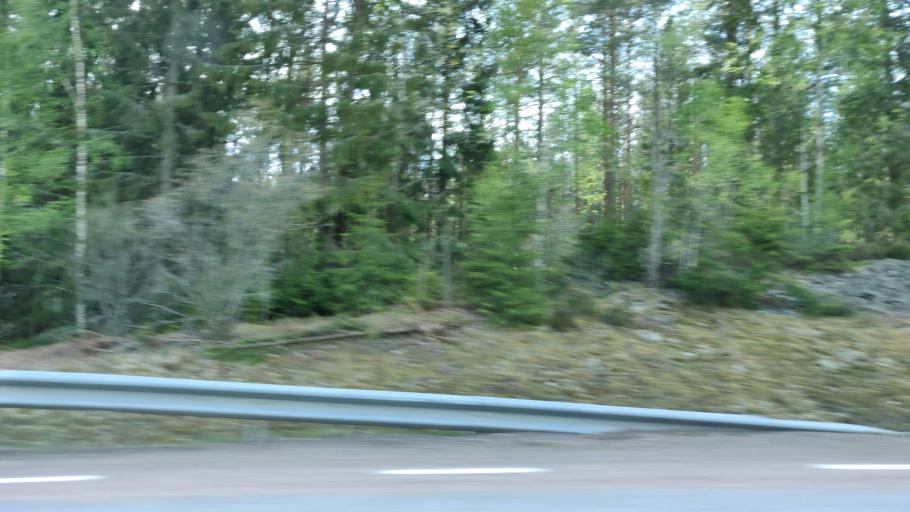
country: SE
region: Vaermland
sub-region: Forshaga Kommun
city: Forshaga
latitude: 59.5349
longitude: 13.4562
